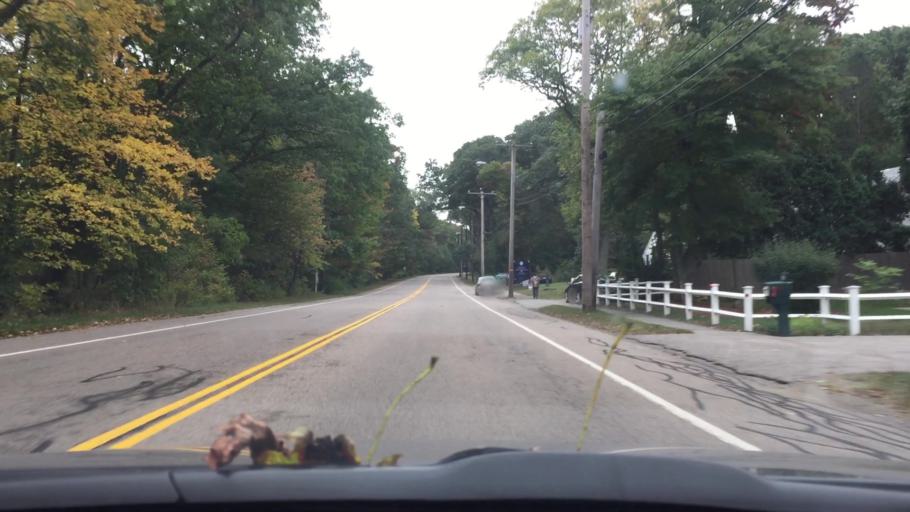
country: US
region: Massachusetts
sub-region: Norfolk County
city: Needham
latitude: 42.2891
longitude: -71.2129
